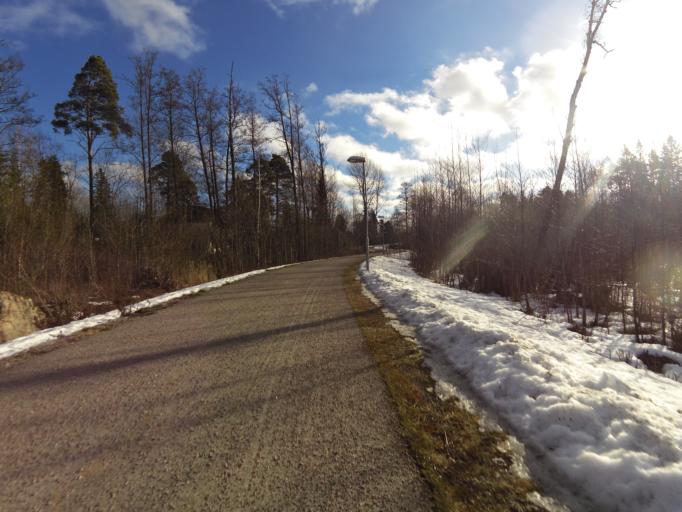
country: SE
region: Uppsala
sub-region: Alvkarleby Kommun
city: Skutskaer
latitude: 60.6510
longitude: 17.3256
